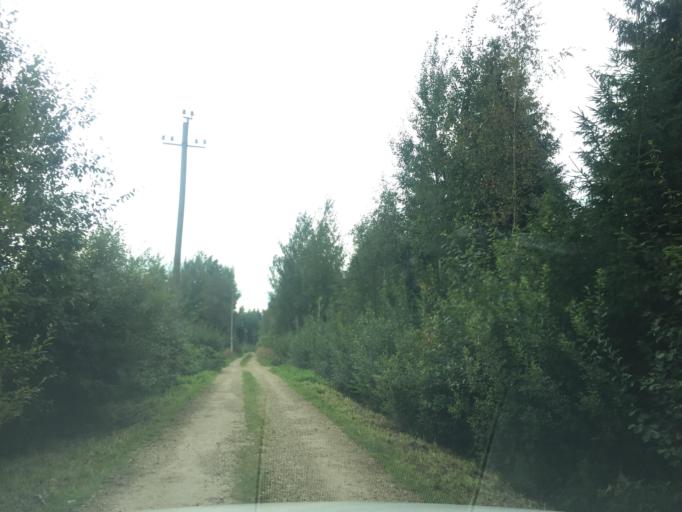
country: RU
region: Leningrad
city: Rozhdestveno
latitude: 59.2973
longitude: 30.0132
